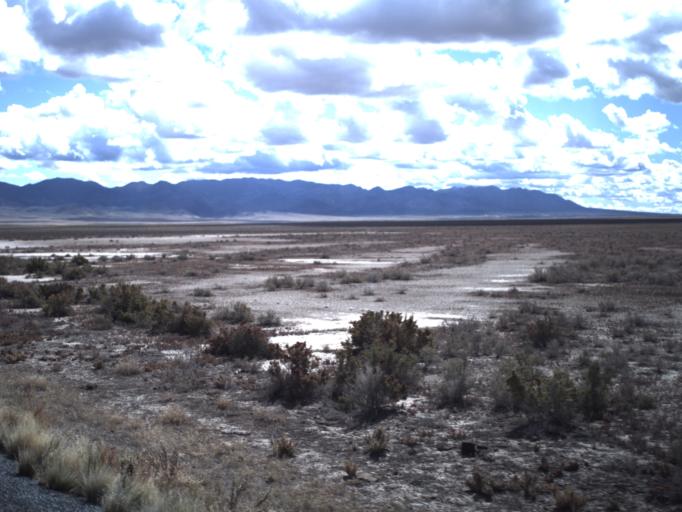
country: US
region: Utah
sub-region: Beaver County
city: Milford
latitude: 38.5499
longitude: -113.7294
